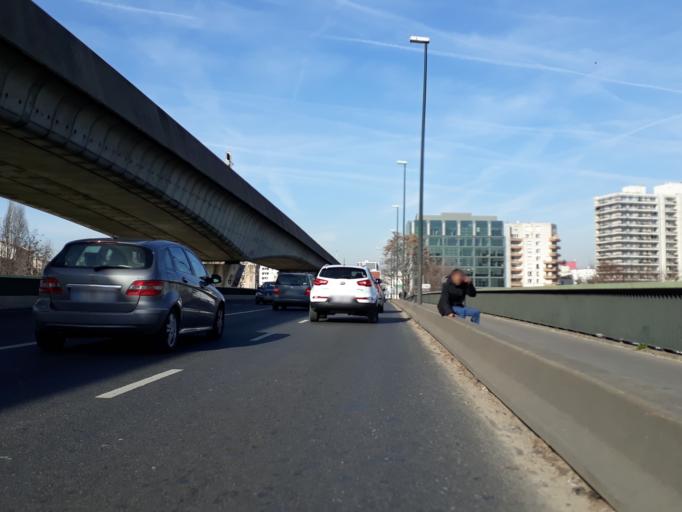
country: FR
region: Ile-de-France
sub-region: Departement des Hauts-de-Seine
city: Clichy
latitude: 48.9094
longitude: 2.2997
